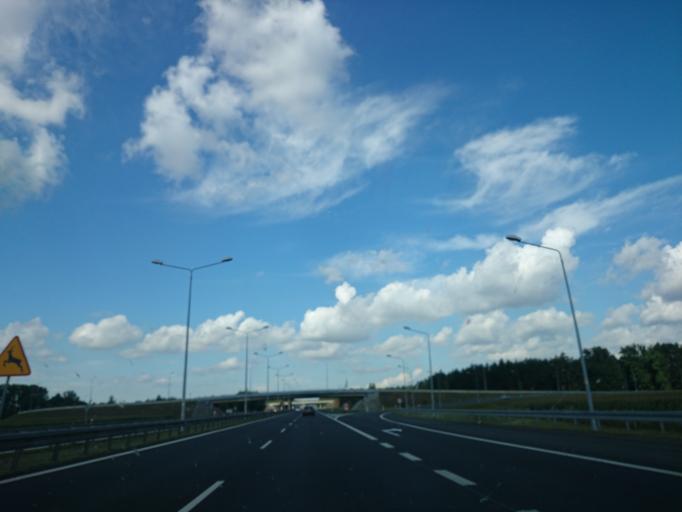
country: PL
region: Opole Voivodeship
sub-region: Powiat opolski
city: Dabrowa
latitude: 50.6603
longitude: 17.7017
